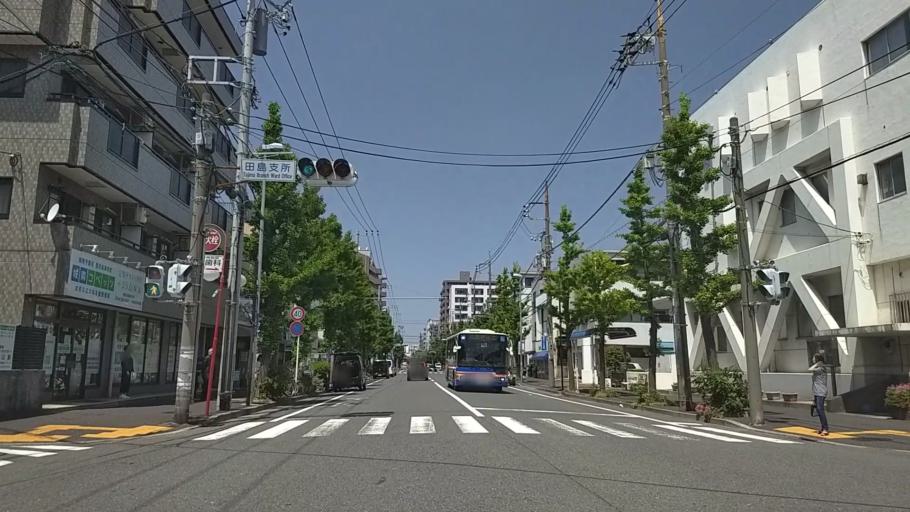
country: JP
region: Kanagawa
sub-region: Kawasaki-shi
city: Kawasaki
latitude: 35.5167
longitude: 139.7142
